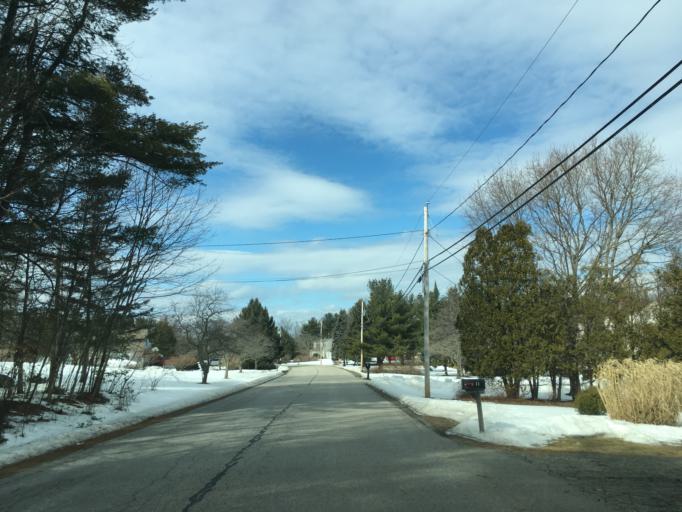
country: US
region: New Hampshire
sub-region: Rockingham County
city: Exeter
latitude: 42.9865
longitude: -70.8901
